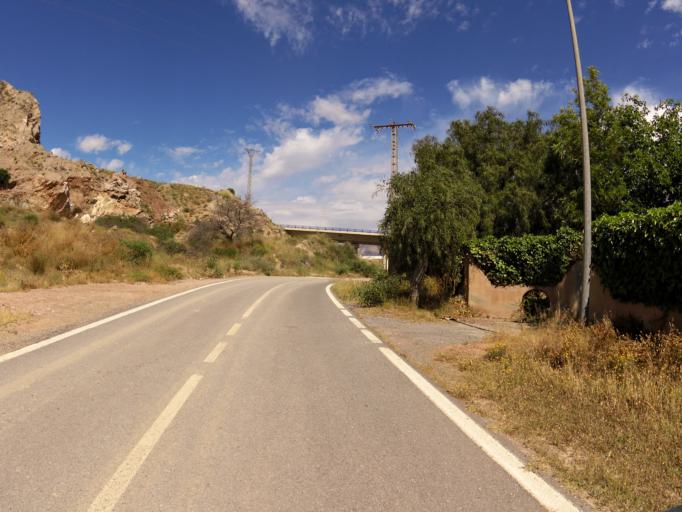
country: ES
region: Valencia
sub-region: Provincia de Alicante
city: Agost
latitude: 38.3960
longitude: -0.6086
